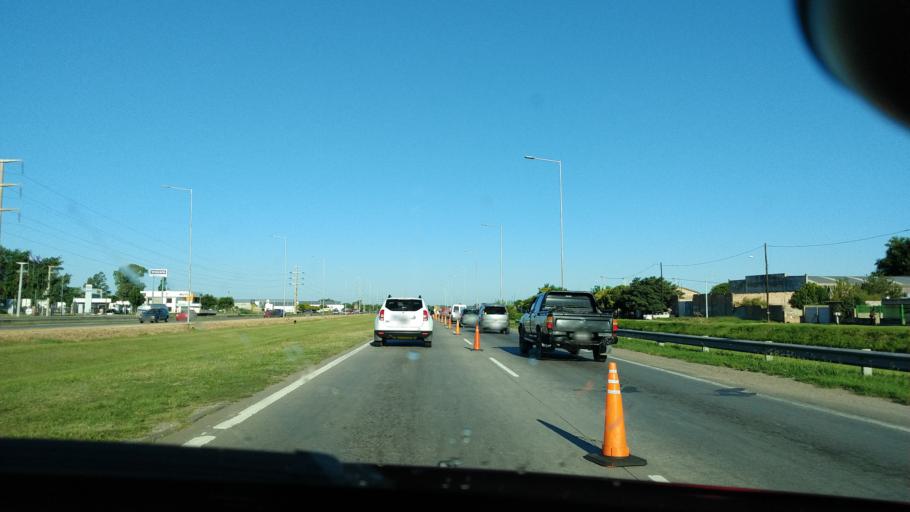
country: AR
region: Cordoba
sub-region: Departamento de Capital
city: Cordoba
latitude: -31.3633
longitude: -64.1413
